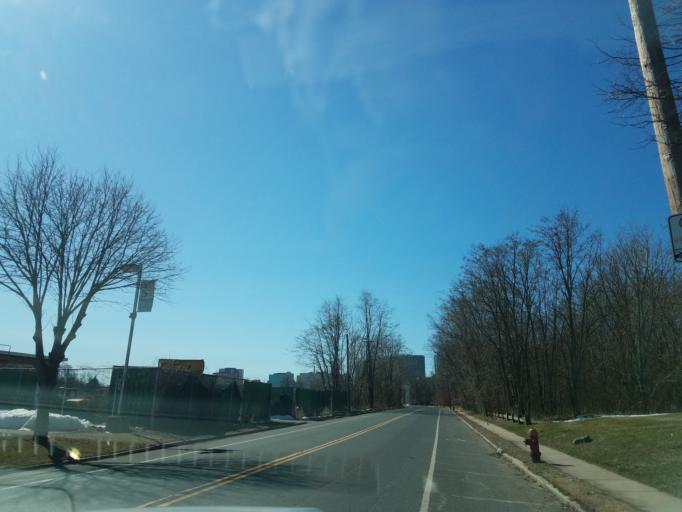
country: US
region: Connecticut
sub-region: Hartford County
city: Hartford
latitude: 41.7806
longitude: -72.6720
